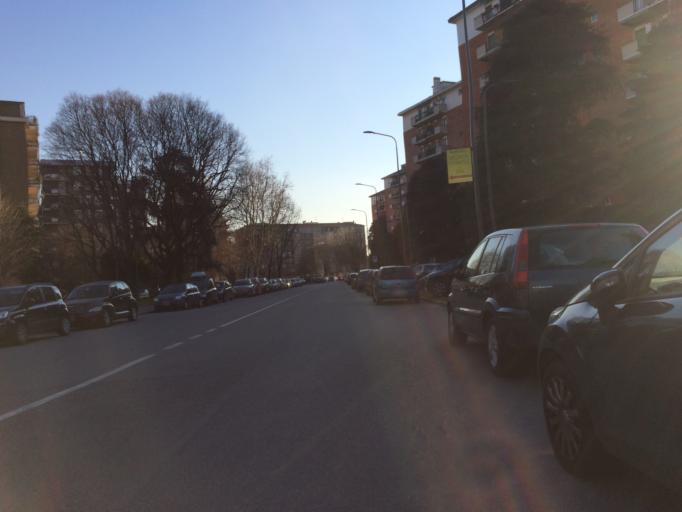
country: IT
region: Lombardy
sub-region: Citta metropolitana di Milano
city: Romano Banco
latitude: 45.4543
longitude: 9.1359
